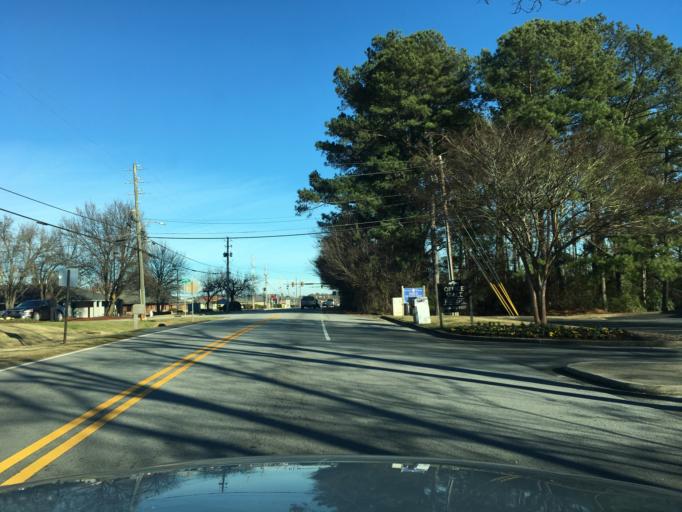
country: US
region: Georgia
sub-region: Rockdale County
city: Conyers
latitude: 33.6647
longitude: -84.0373
